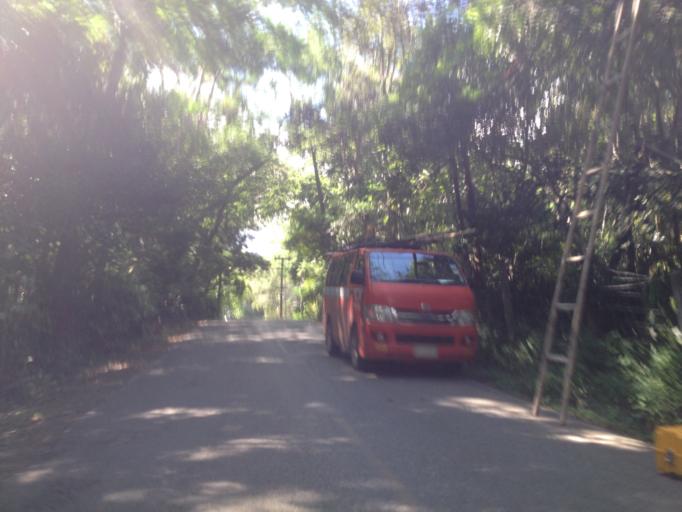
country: TH
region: Chiang Mai
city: Chiang Mai
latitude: 18.7947
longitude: 98.9479
